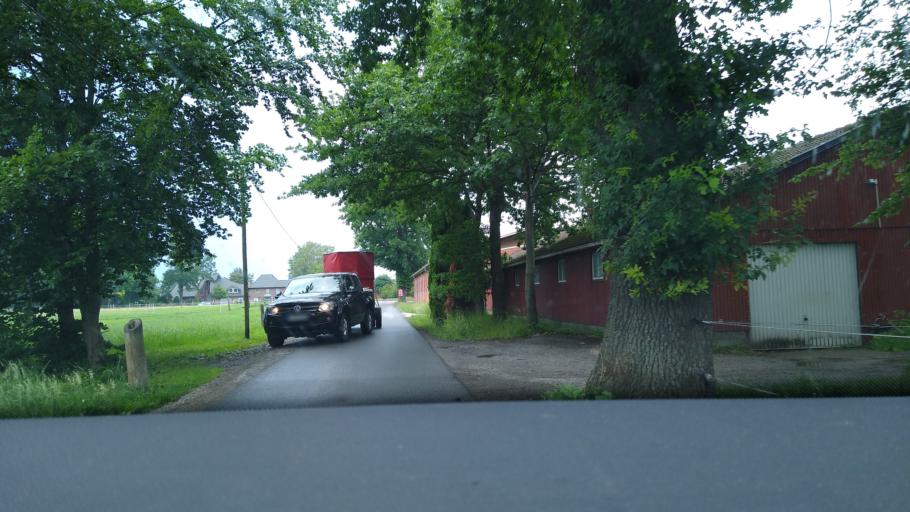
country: DE
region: North Rhine-Westphalia
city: Rietberg
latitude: 51.8436
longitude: 8.4355
